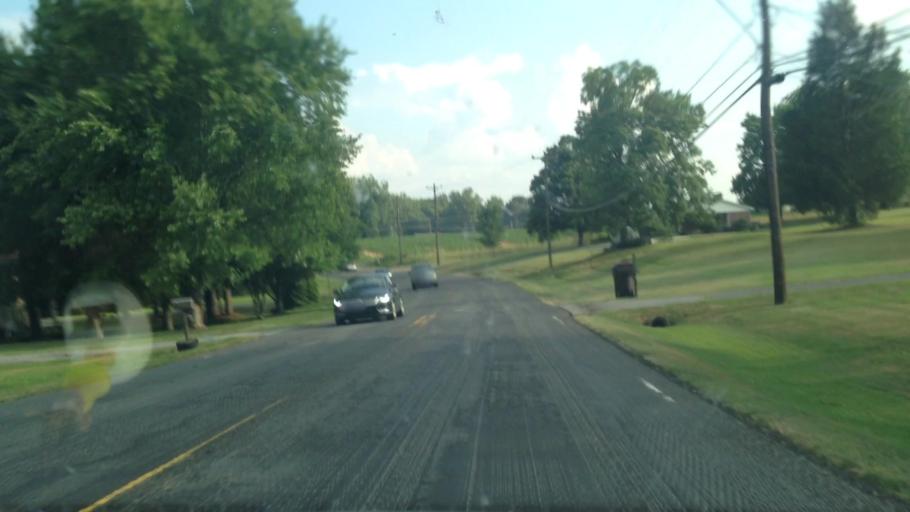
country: US
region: North Carolina
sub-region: Forsyth County
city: Kernersville
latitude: 36.0535
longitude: -80.0655
